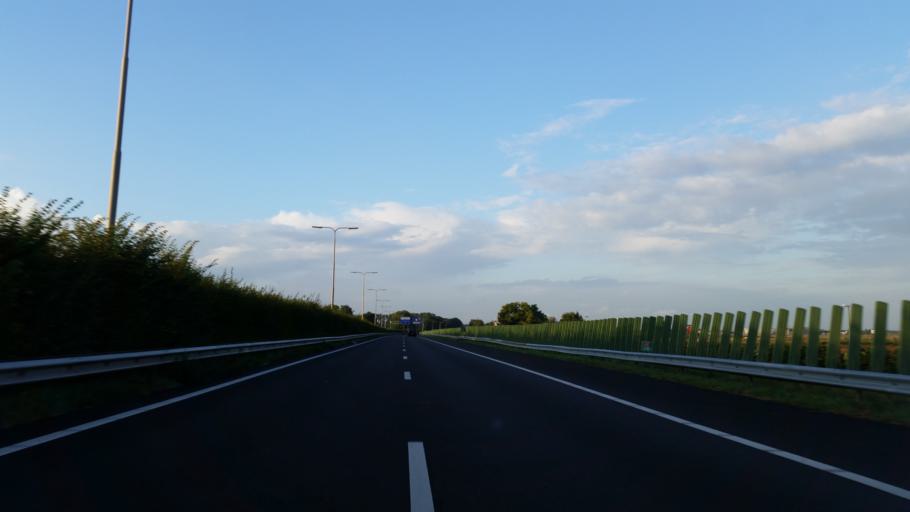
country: NL
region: Limburg
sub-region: Gemeente Meerssen
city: Meerssen
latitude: 50.9076
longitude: 5.7601
